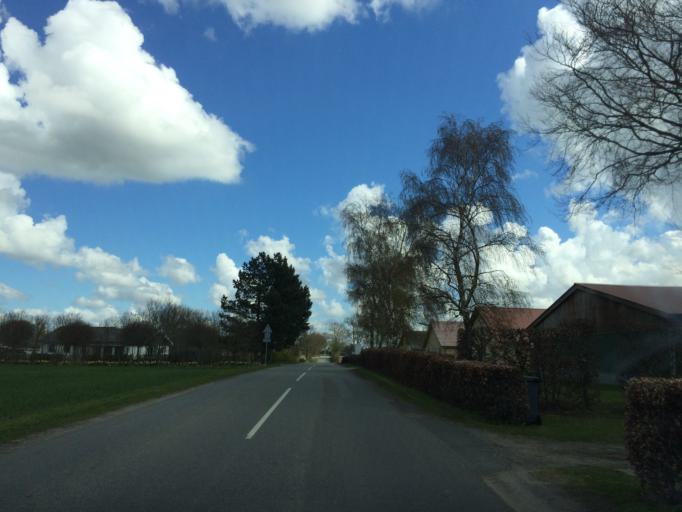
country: DK
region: South Denmark
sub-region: Odense Kommune
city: Bellinge
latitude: 55.2649
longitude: 10.2932
